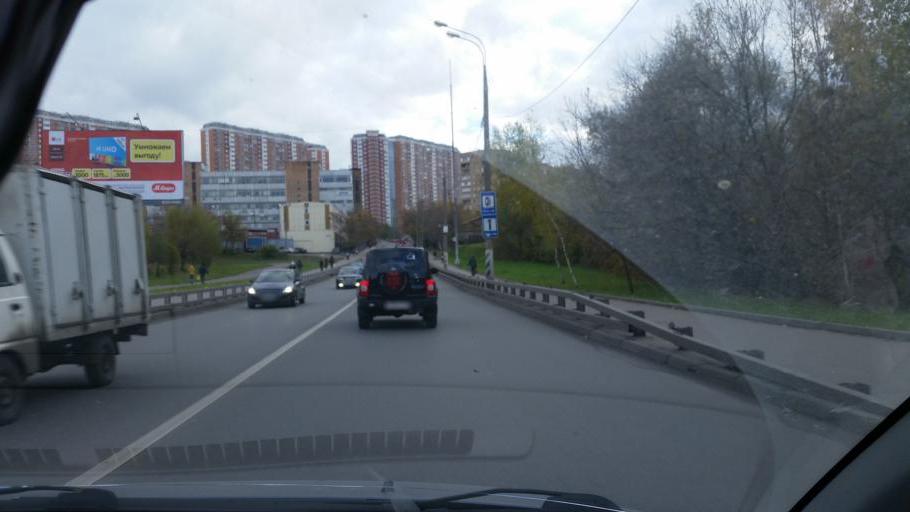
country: RU
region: Moscow
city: Kotlovka
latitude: 55.6742
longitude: 37.6050
